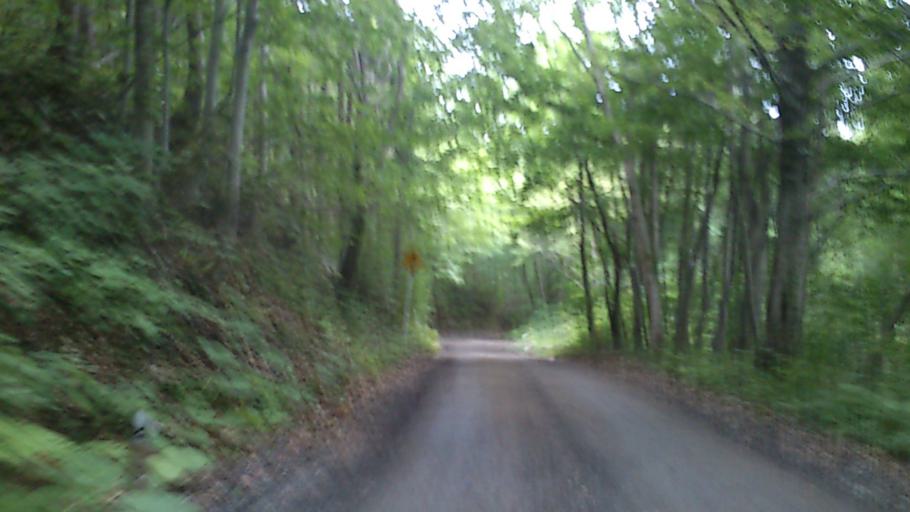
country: JP
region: Aomori
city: Hirosaki
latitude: 40.5494
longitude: 140.1807
